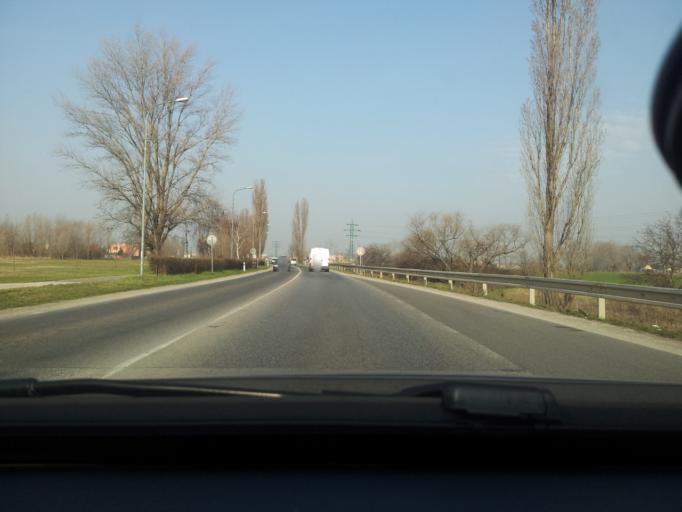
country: SK
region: Trnavsky
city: Hlohovec
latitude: 48.4342
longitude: 17.7835
